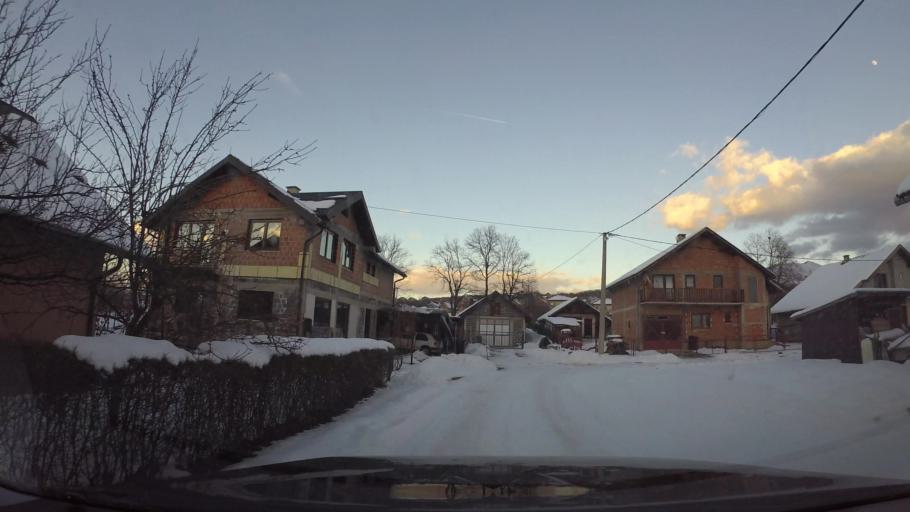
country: BA
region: Federation of Bosnia and Herzegovina
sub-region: Kanton Sarajevo
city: Sarajevo
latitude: 43.8079
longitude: 18.3736
